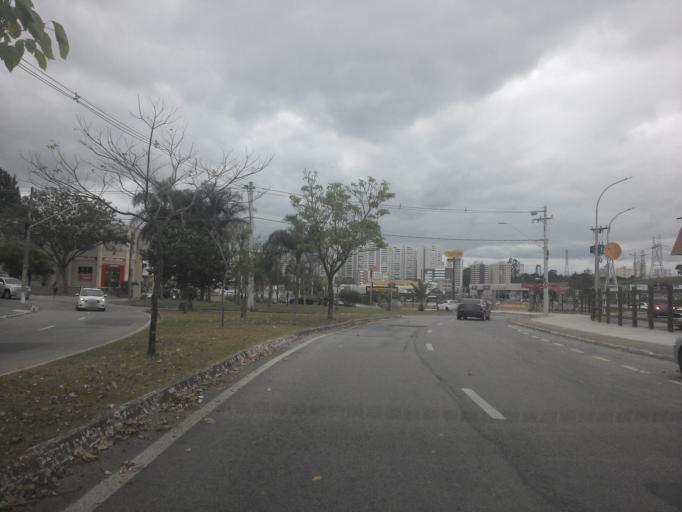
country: BR
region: Sao Paulo
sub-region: Sao Jose Dos Campos
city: Sao Jose dos Campos
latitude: -23.2165
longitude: -45.9025
